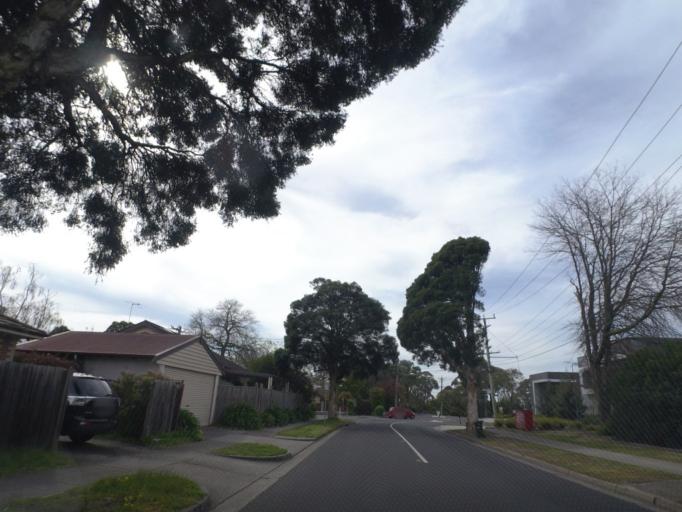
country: AU
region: Victoria
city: Mitcham
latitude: -37.8124
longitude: 145.2021
